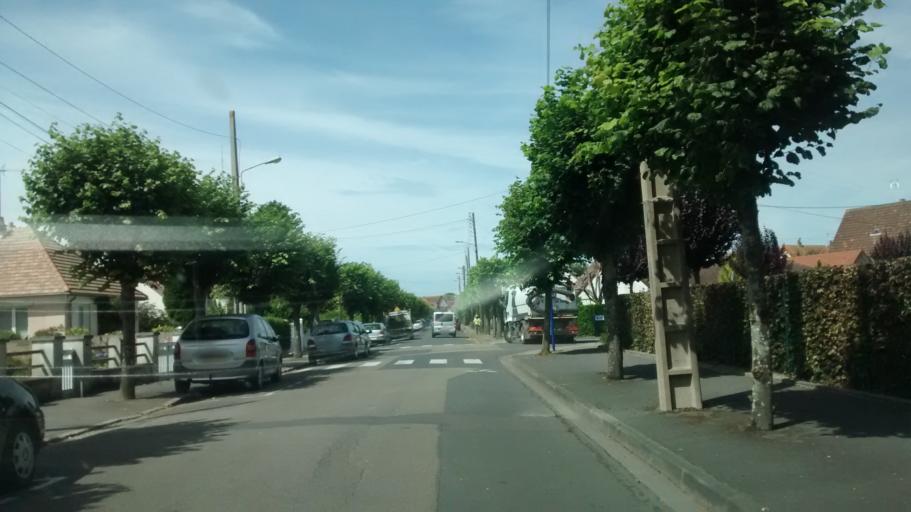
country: FR
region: Lower Normandy
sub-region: Departement du Calvados
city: Ouistreham
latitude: 49.2793
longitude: -0.2573
